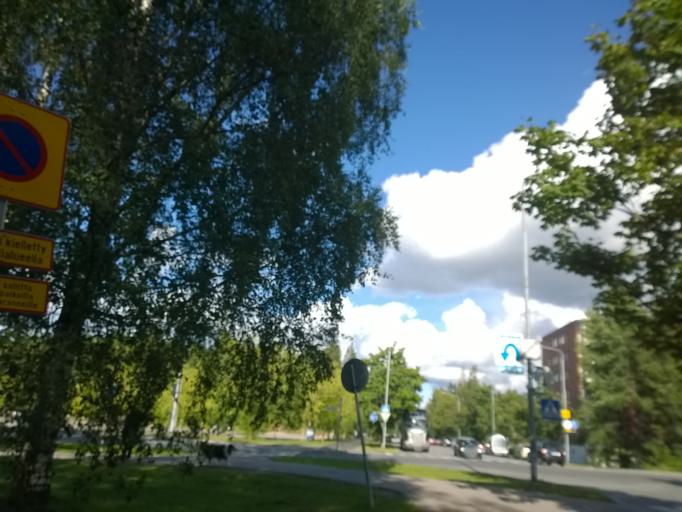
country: FI
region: Pirkanmaa
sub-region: Tampere
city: Tampere
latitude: 61.4473
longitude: 23.8348
